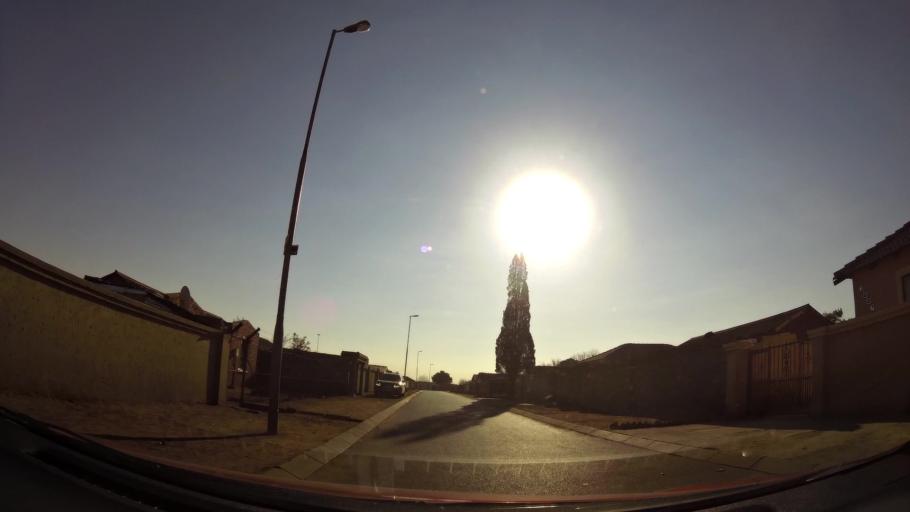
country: ZA
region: Gauteng
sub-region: City of Johannesburg Metropolitan Municipality
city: Soweto
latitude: -26.2347
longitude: 27.9353
